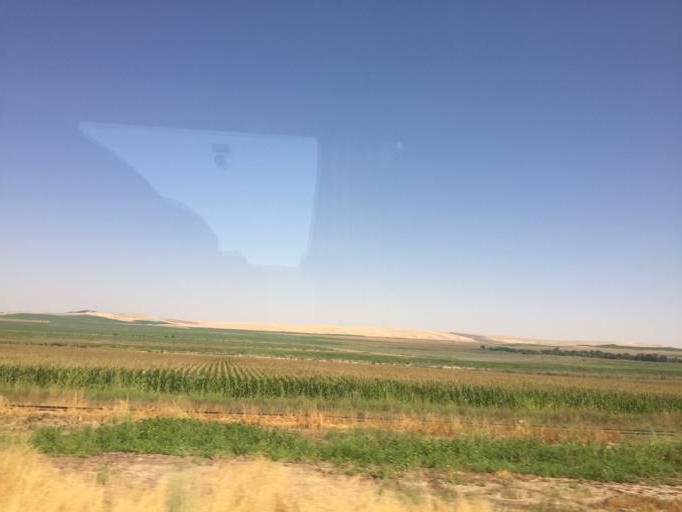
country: TR
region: Diyarbakir
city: Tepe
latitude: 37.8492
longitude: 40.7919
